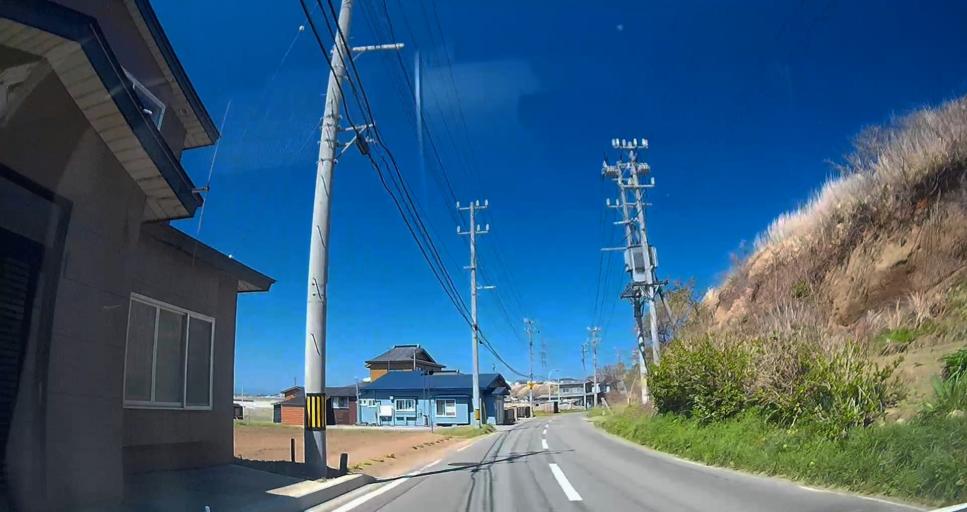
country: JP
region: Hokkaido
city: Hakodate
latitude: 41.5005
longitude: 140.9085
